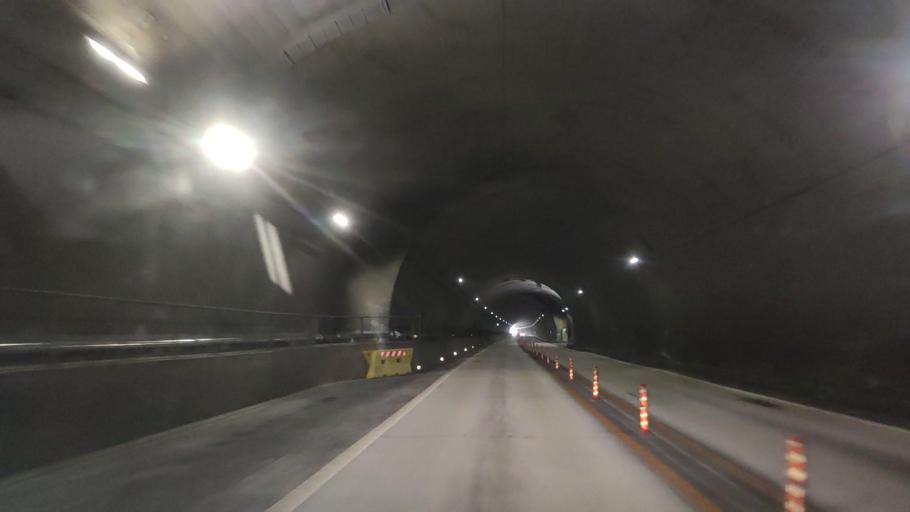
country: JP
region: Ehime
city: Hojo
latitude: 34.0833
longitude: 132.9773
